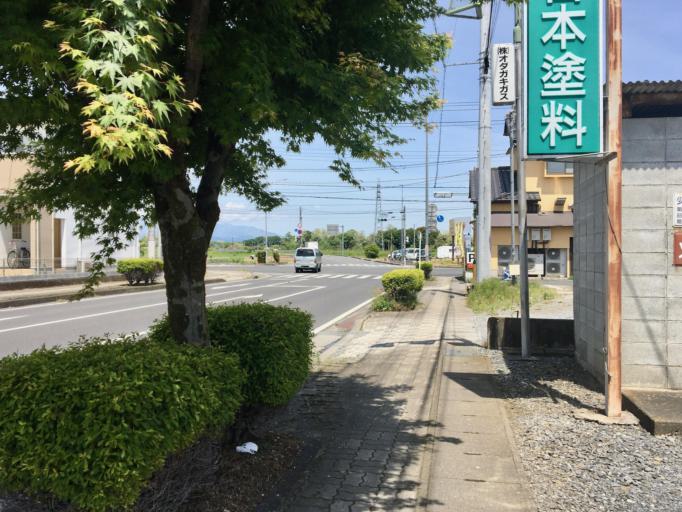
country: JP
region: Tochigi
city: Mibu
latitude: 36.4345
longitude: 139.8021
